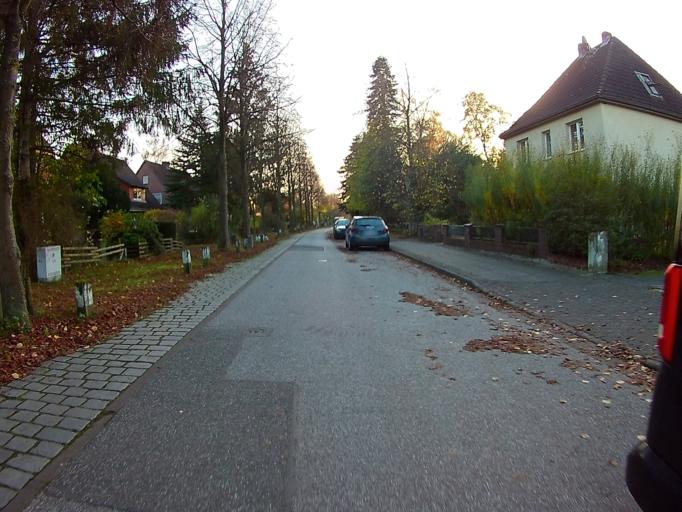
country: DE
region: Hamburg
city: Harburg
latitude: 53.4874
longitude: 9.9349
